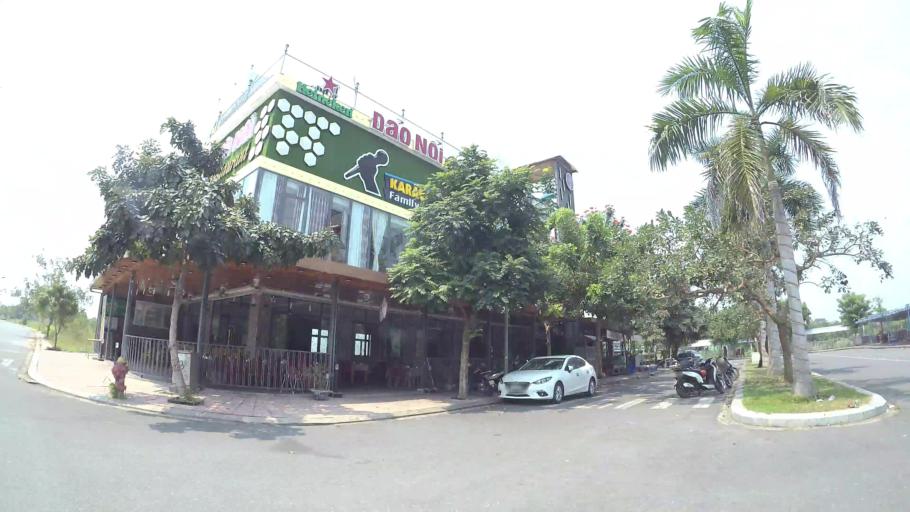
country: VN
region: Da Nang
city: Cam Le
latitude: 16.0165
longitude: 108.2125
